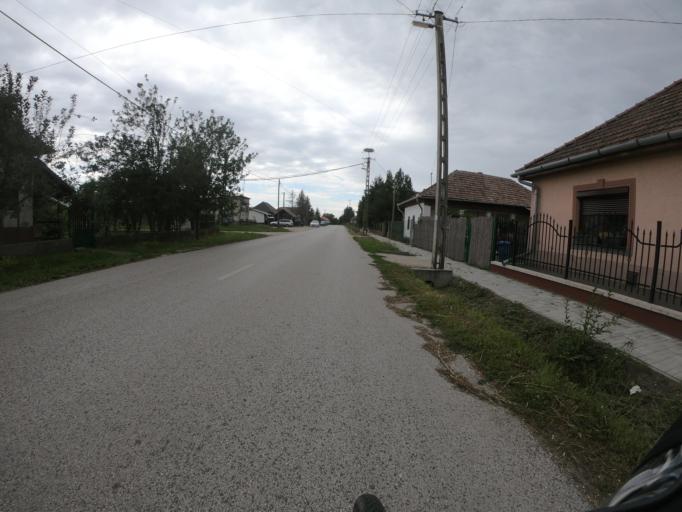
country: HU
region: Heves
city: Poroszlo
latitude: 47.7005
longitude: 20.7076
